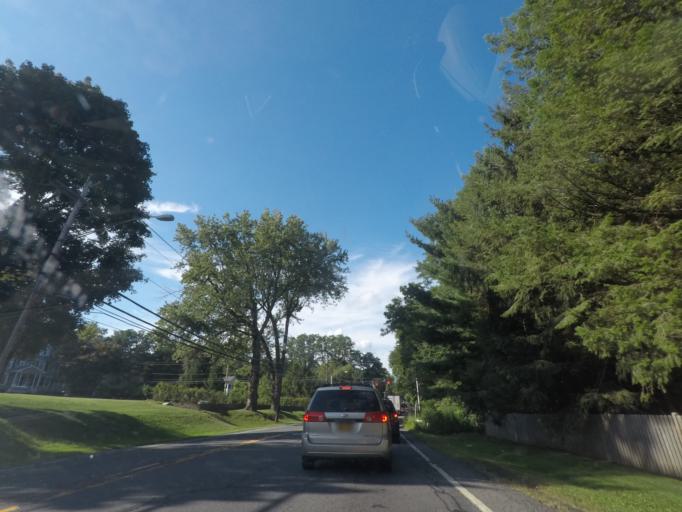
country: US
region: New York
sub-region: Albany County
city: West Albany
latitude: 42.6962
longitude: -73.7541
